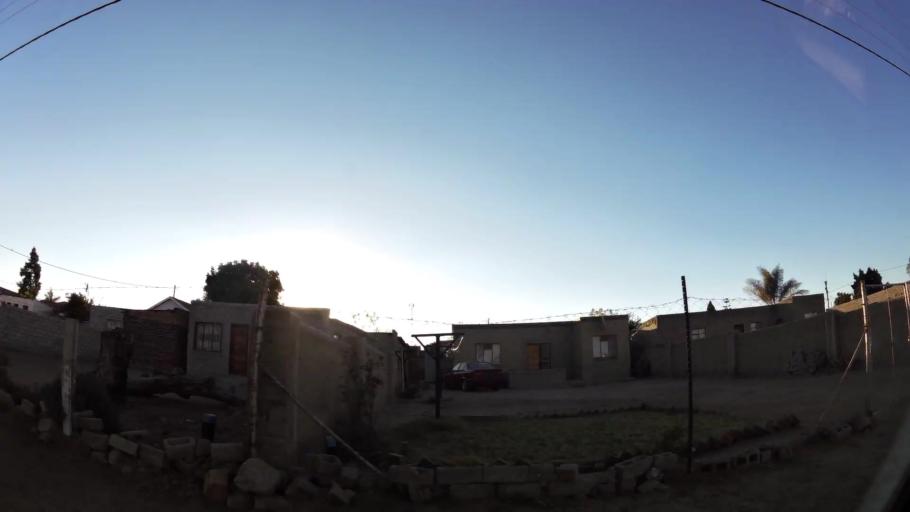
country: ZA
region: Limpopo
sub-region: Capricorn District Municipality
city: Polokwane
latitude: -23.8502
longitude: 29.3544
